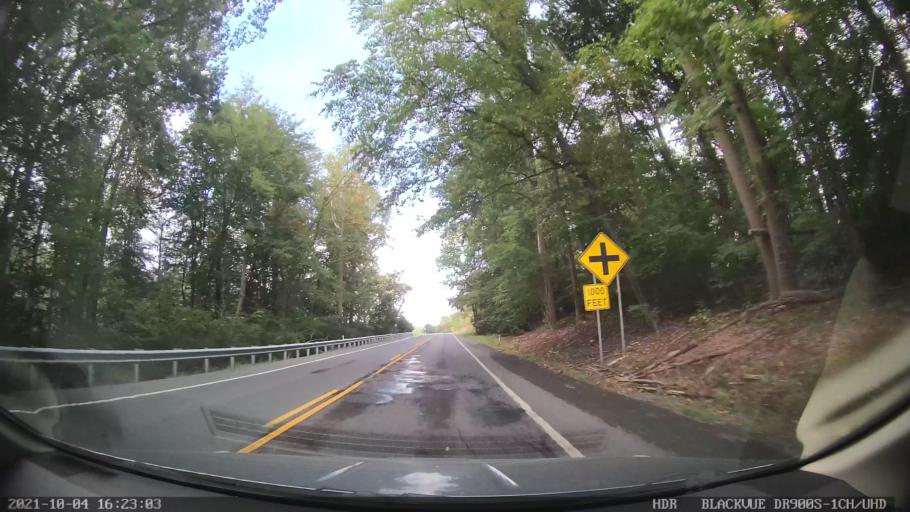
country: US
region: Pennsylvania
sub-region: Berks County
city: Blandon
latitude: 40.4208
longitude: -75.8669
